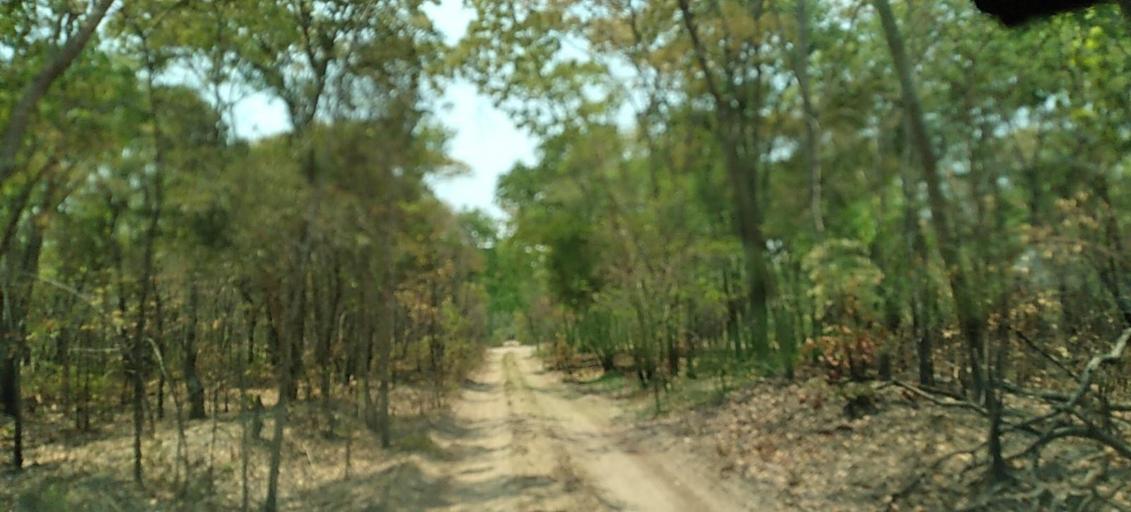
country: ZM
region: North-Western
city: Kabompo
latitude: -13.6461
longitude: 24.4825
